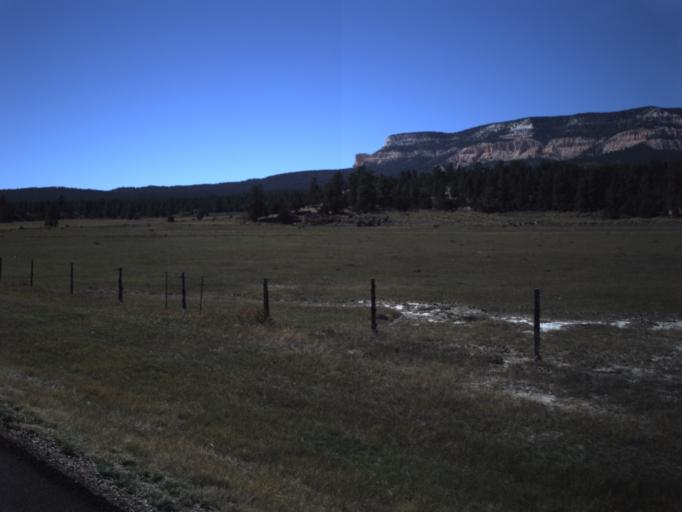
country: US
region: Utah
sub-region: Garfield County
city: Panguitch
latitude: 37.6869
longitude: -111.8072
